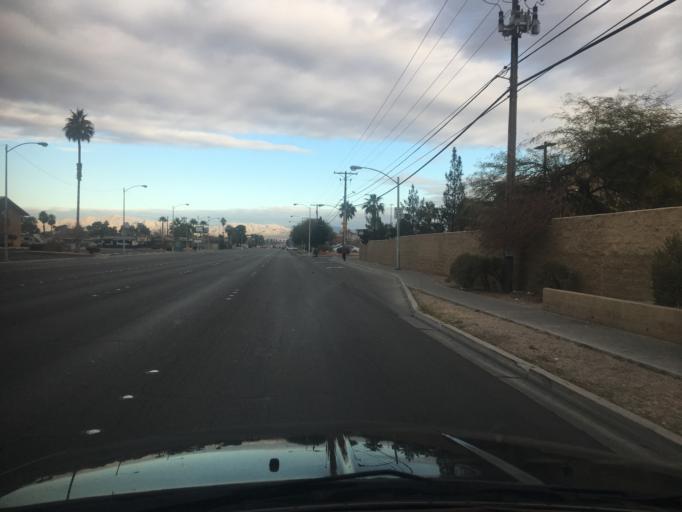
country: US
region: Nevada
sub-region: Clark County
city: Whitney
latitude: 36.1083
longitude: -115.0643
